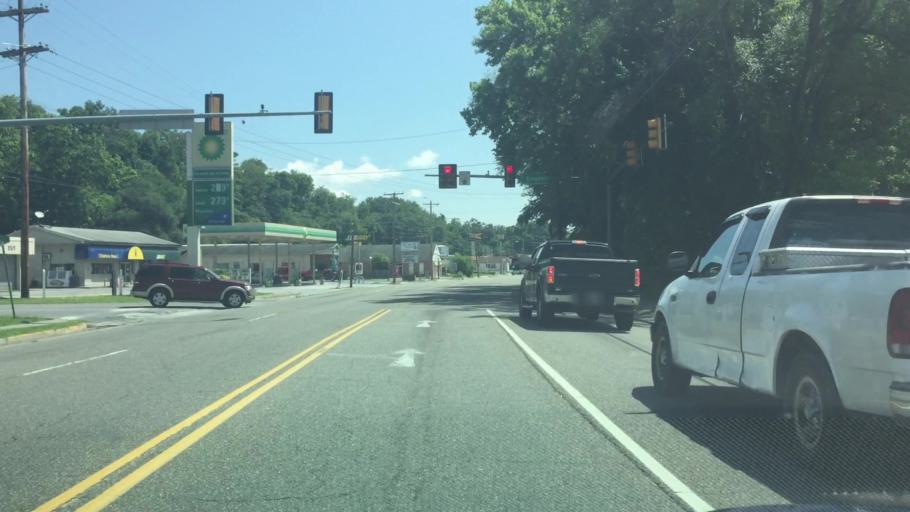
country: US
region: Virginia
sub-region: Pulaski County
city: Pulaski
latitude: 37.0485
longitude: -80.7710
